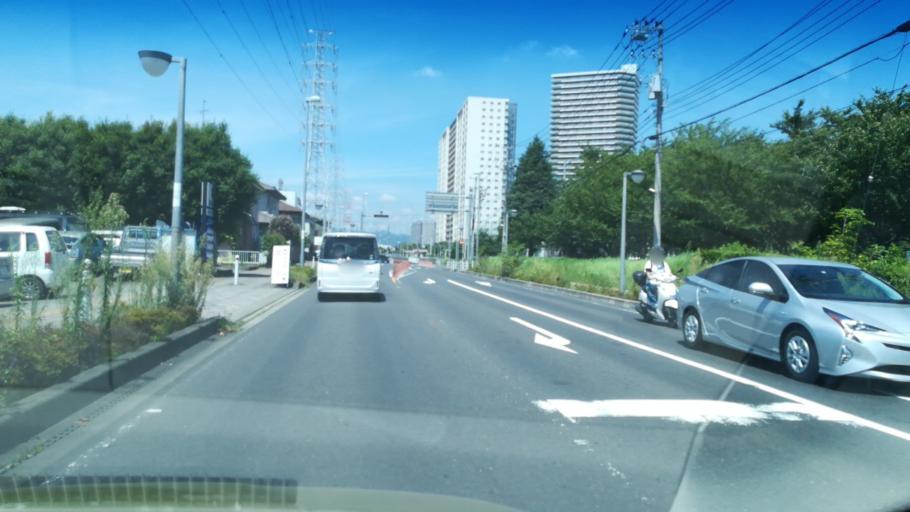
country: JP
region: Tokyo
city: Hachioji
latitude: 35.5873
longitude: 139.3553
